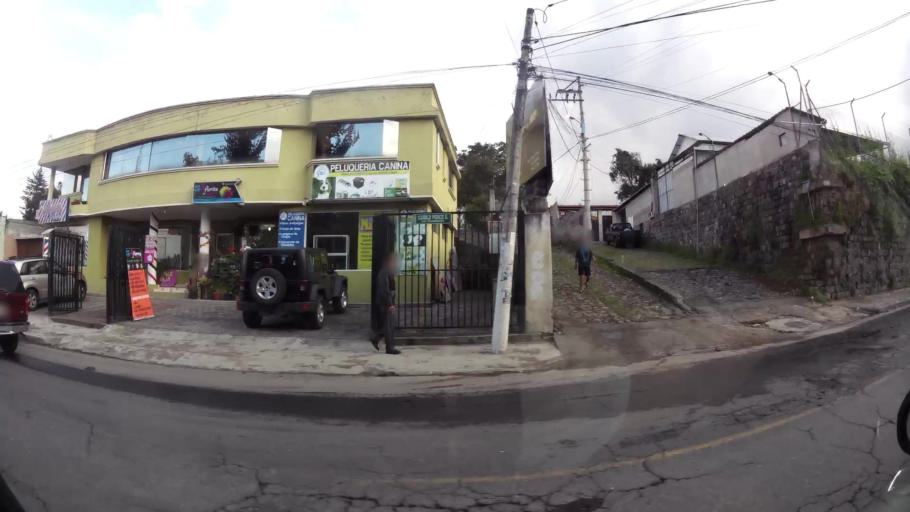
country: EC
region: Pichincha
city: Sangolqui
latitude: -0.2926
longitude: -78.4805
